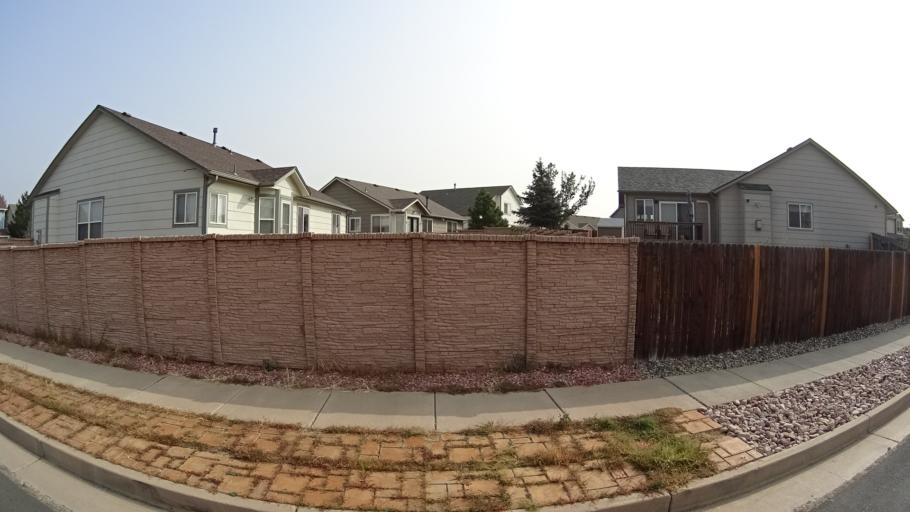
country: US
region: Colorado
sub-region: El Paso County
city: Black Forest
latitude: 38.9365
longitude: -104.7288
